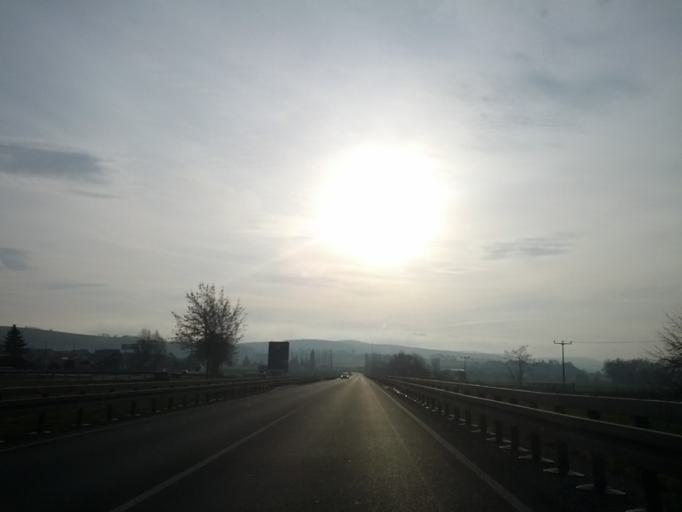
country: DE
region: Thuringia
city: Fambach
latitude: 50.7383
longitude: 10.3590
